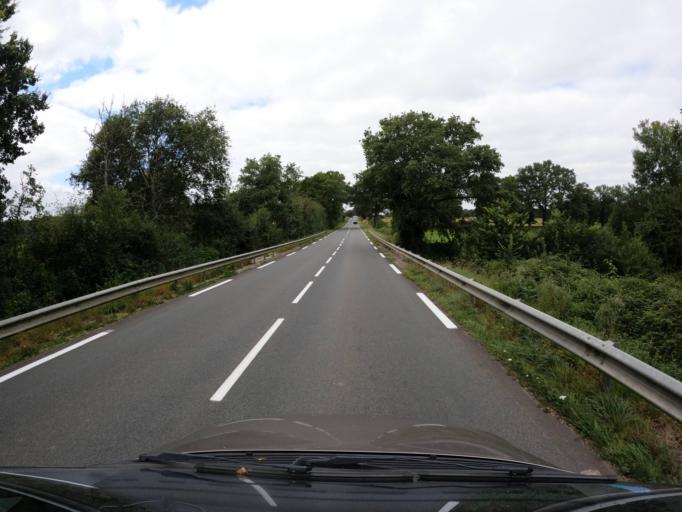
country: FR
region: Poitou-Charentes
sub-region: Departement de la Vienne
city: Charroux
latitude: 46.1214
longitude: 0.5214
